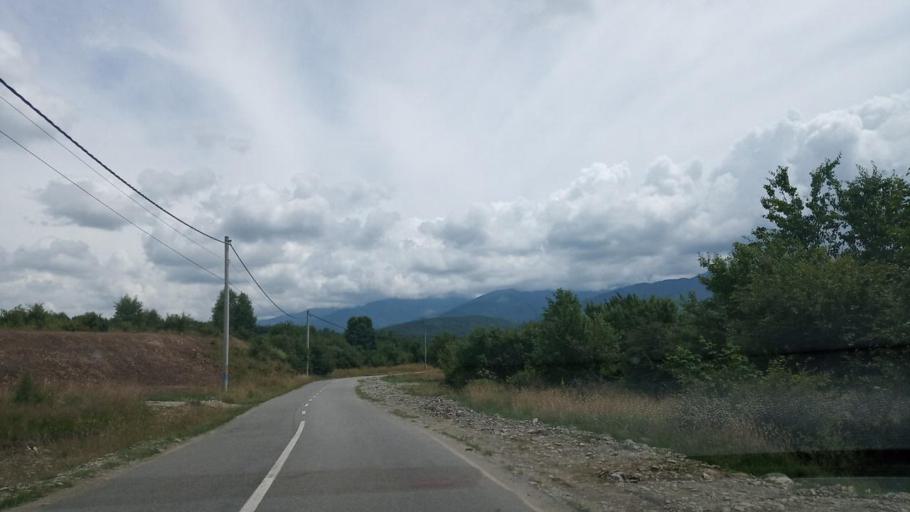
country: RO
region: Sibiu
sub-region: Comuna Porumbacu de Jos
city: Porumbacu de Jos
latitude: 45.6996
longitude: 24.4889
